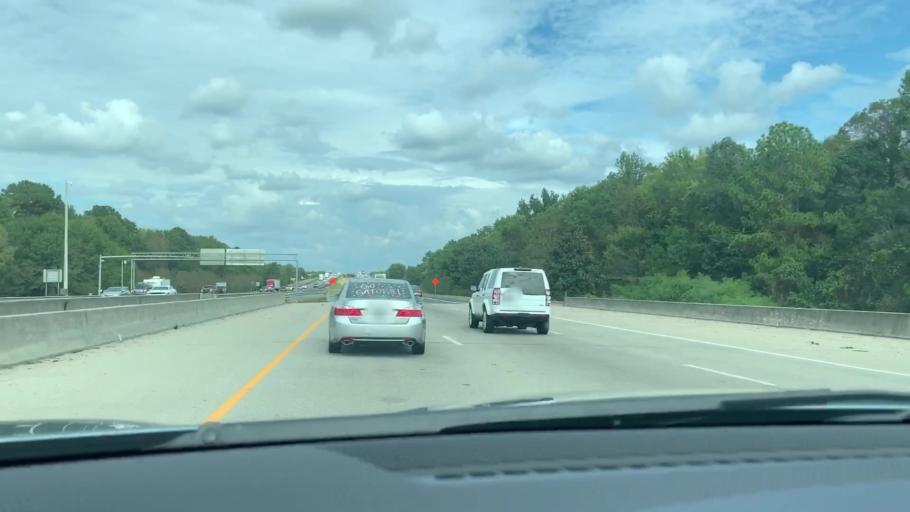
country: US
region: Georgia
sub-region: Chatham County
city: Port Wentworth
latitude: 32.2298
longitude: -81.1592
